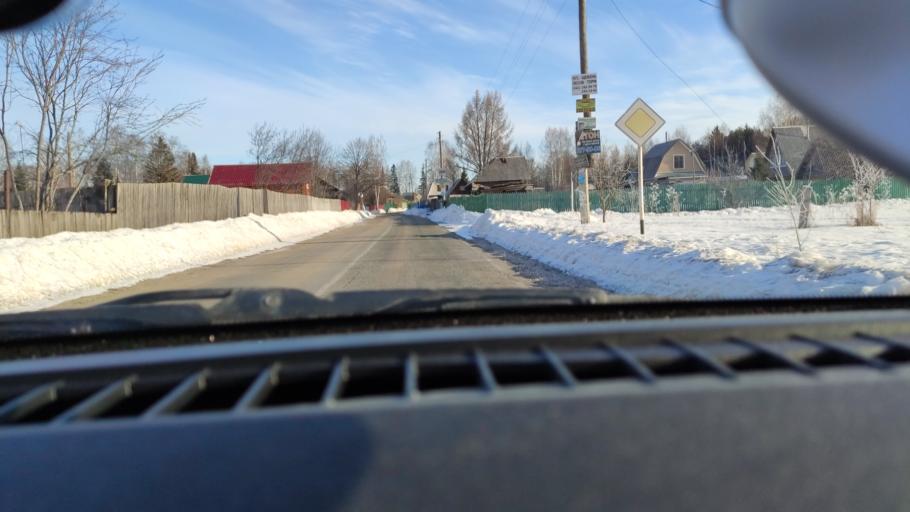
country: RU
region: Perm
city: Ust'-Kachka
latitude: 58.0127
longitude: 55.6057
